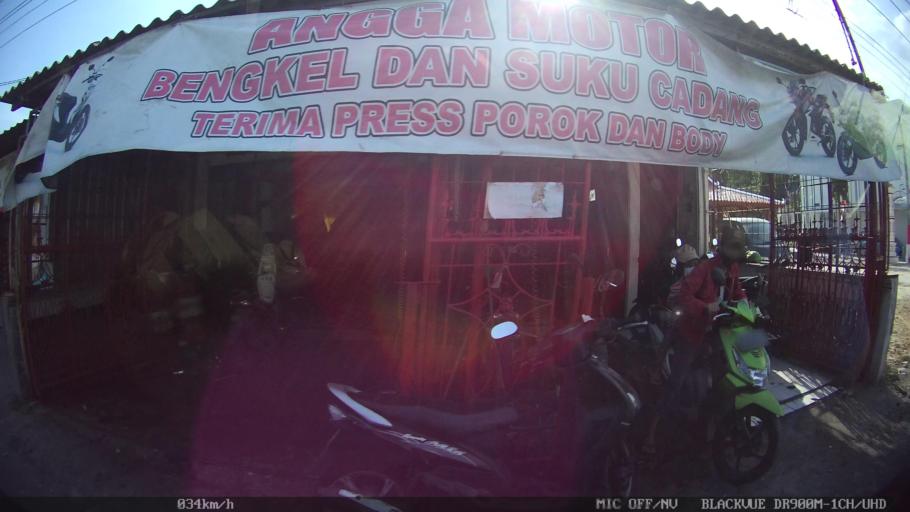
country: ID
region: Daerah Istimewa Yogyakarta
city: Kasihan
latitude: -7.8359
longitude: 110.3440
